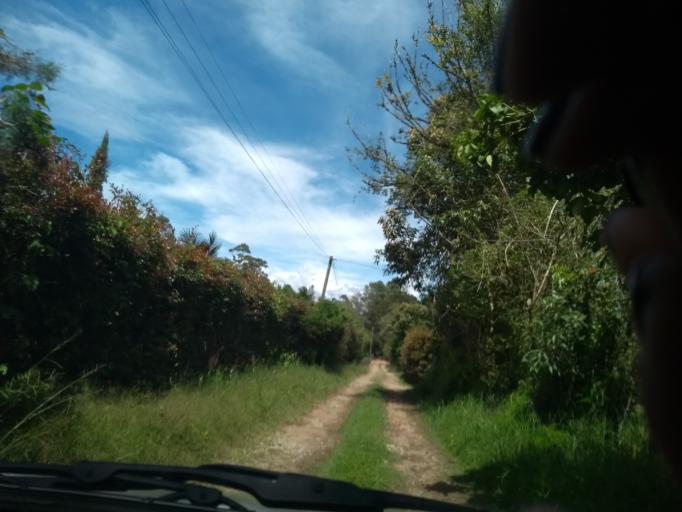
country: CO
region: Antioquia
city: Rionegro
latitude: 6.1057
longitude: -75.3969
